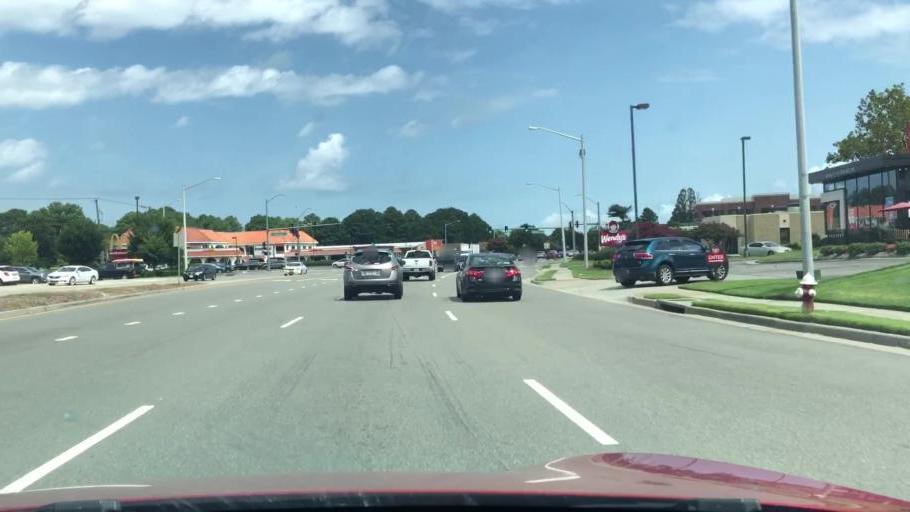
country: US
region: Virginia
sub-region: City of Chesapeake
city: Chesapeake
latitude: 36.8742
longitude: -76.1344
